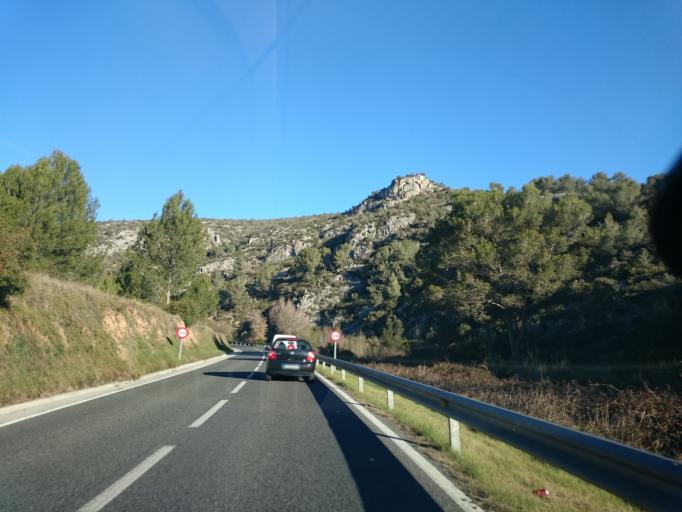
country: ES
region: Catalonia
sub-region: Provincia de Barcelona
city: Sant Pere de Ribes
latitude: 41.2891
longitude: 1.7373
